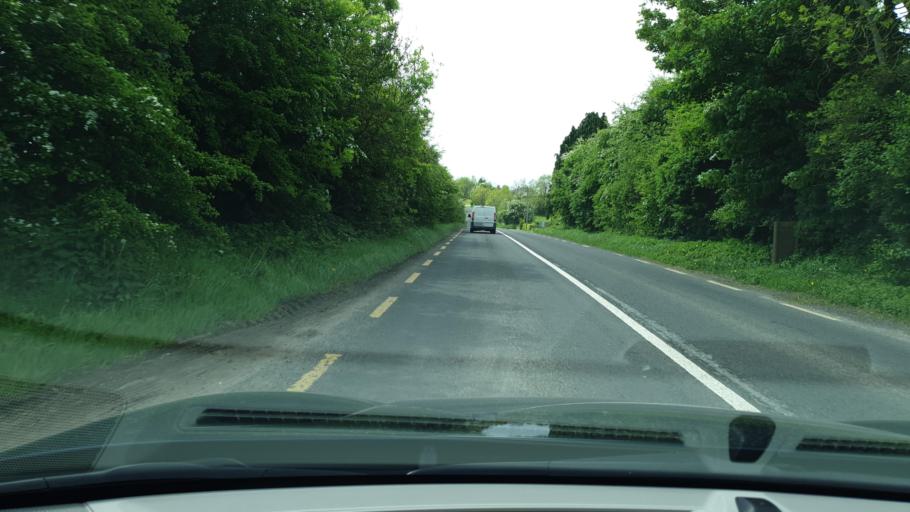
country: IE
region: Ulster
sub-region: An Cabhan
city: Kingscourt
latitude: 53.8014
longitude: -6.7374
